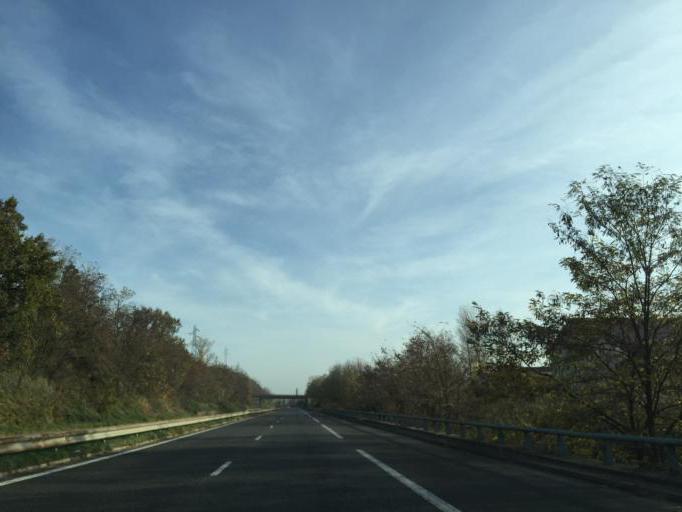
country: FR
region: Rhone-Alpes
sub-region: Departement de la Loire
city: La Grand-Croix
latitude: 45.4882
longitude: 4.5417
